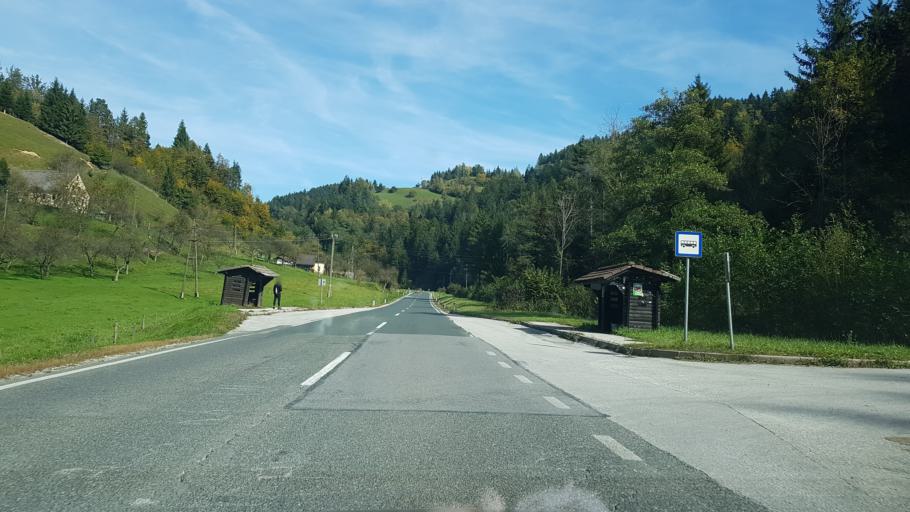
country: SI
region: Velenje
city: Velenje
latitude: 46.3967
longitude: 15.1732
